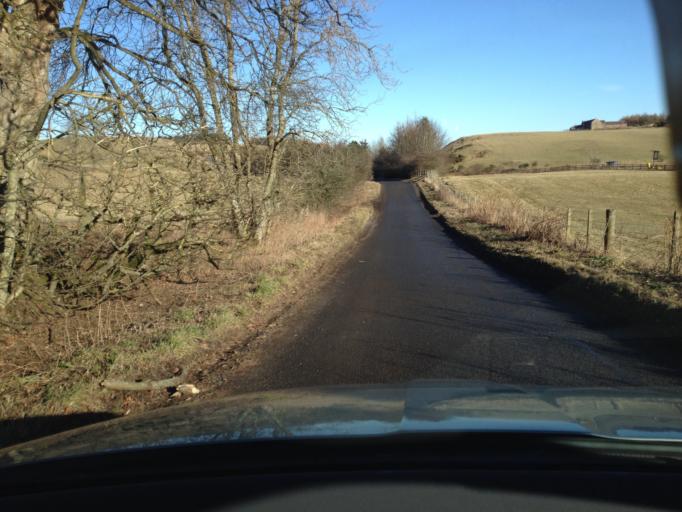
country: GB
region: Scotland
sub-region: Perth and Kinross
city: Bridge of Earn
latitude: 56.3020
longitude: -3.3877
